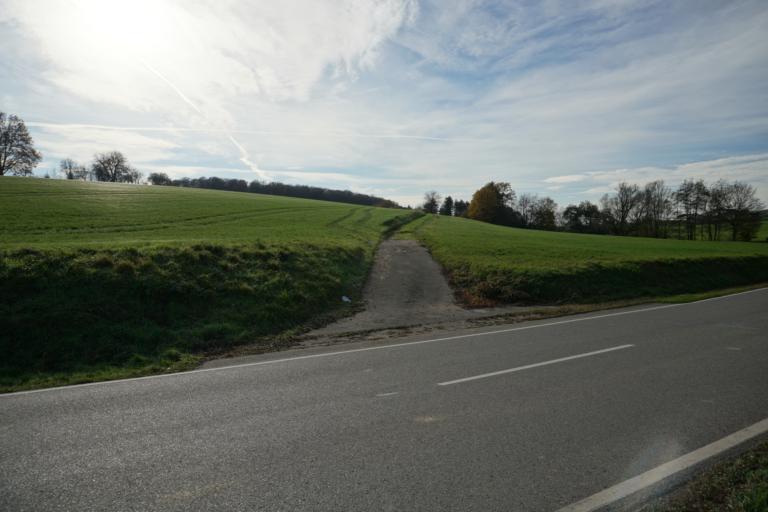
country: DE
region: Baden-Wuerttemberg
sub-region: Karlsruhe Region
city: Neunkirchen
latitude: 49.3646
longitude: 9.0174
